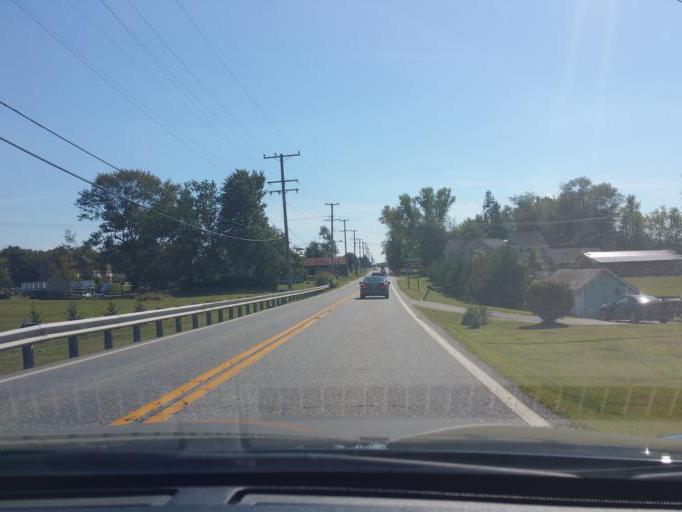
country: US
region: Maryland
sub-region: Harford County
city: Aberdeen
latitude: 39.5831
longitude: -76.1845
